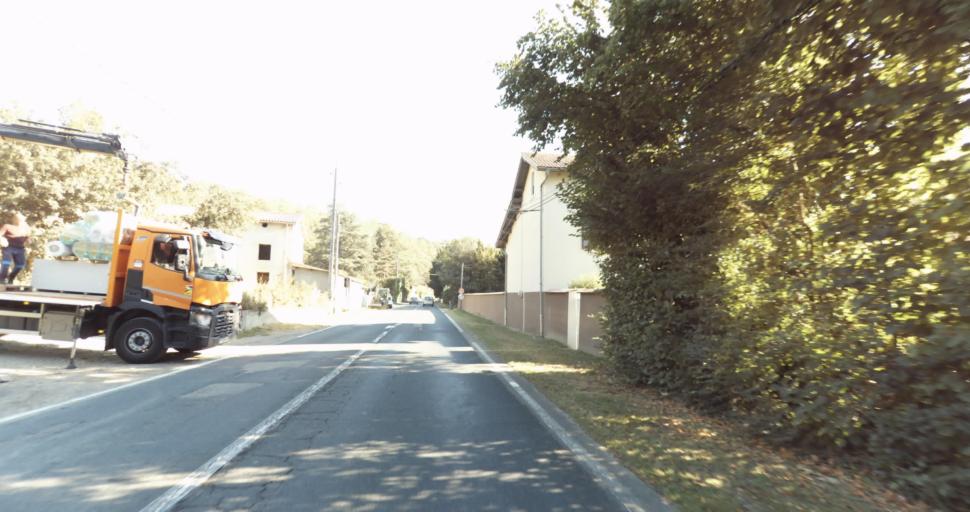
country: FR
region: Rhone-Alpes
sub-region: Departement du Rhone
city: Neuville-sur-Saone
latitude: 45.8873
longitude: 4.8508
